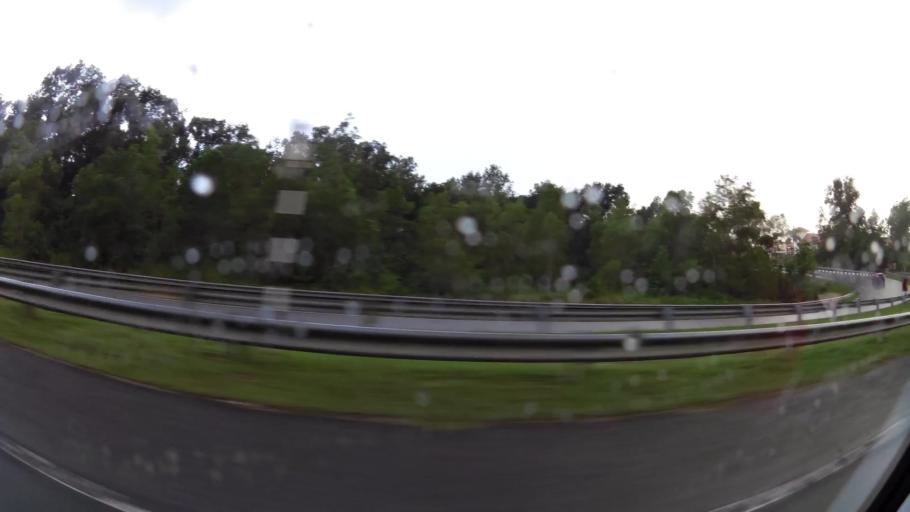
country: BN
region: Brunei and Muara
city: Bandar Seri Begawan
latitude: 4.9265
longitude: 114.9638
